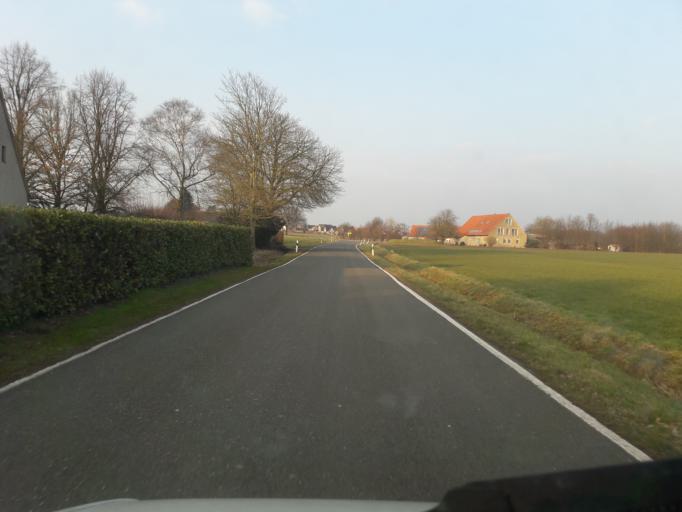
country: DE
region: North Rhine-Westphalia
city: Lubbecke
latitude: 52.3386
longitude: 8.6589
